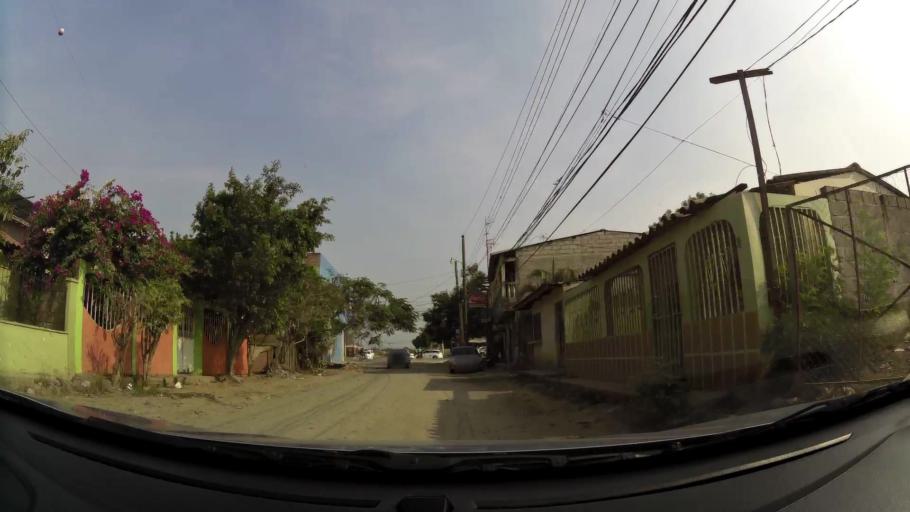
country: HN
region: Comayagua
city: Comayagua
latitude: 14.4458
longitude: -87.6351
